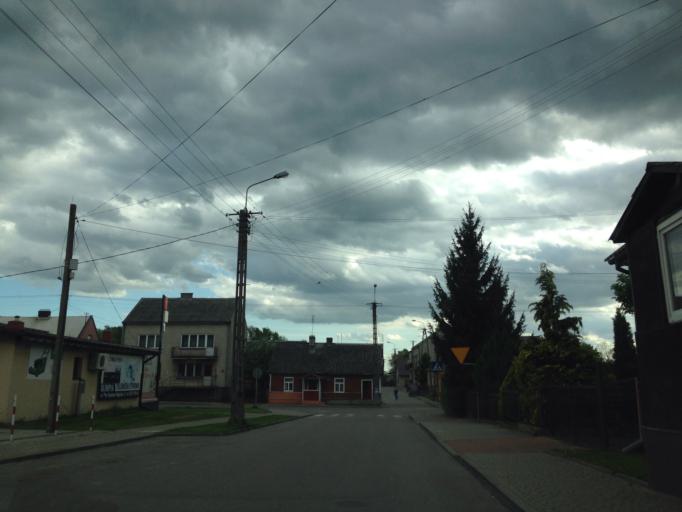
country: PL
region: Podlasie
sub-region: Powiat lomzynski
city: Wizna
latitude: 53.1923
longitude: 22.3846
